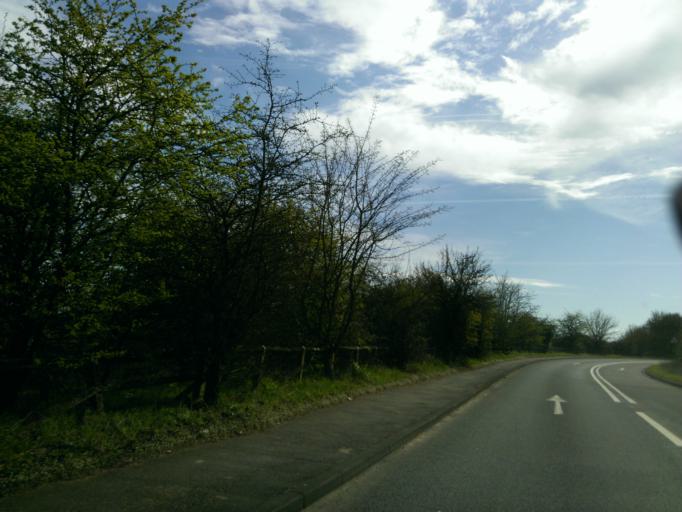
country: GB
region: England
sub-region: Essex
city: Kelvedon
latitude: 51.8488
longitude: 0.7261
